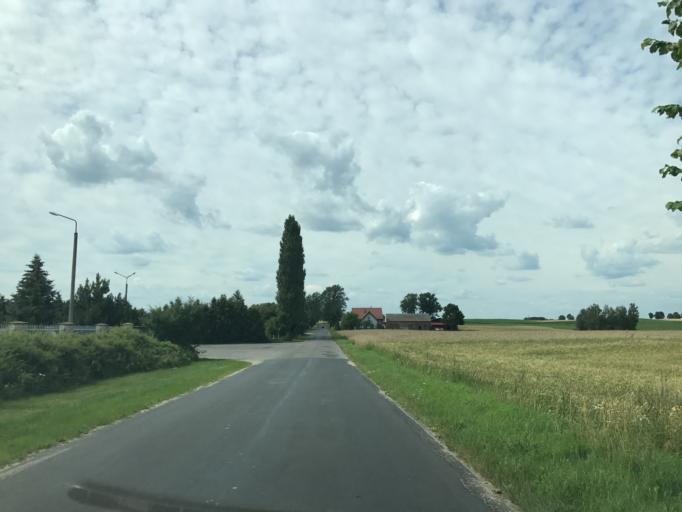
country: PL
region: Kujawsko-Pomorskie
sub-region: Powiat brodnicki
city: Bartniczka
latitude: 53.2188
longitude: 19.6136
